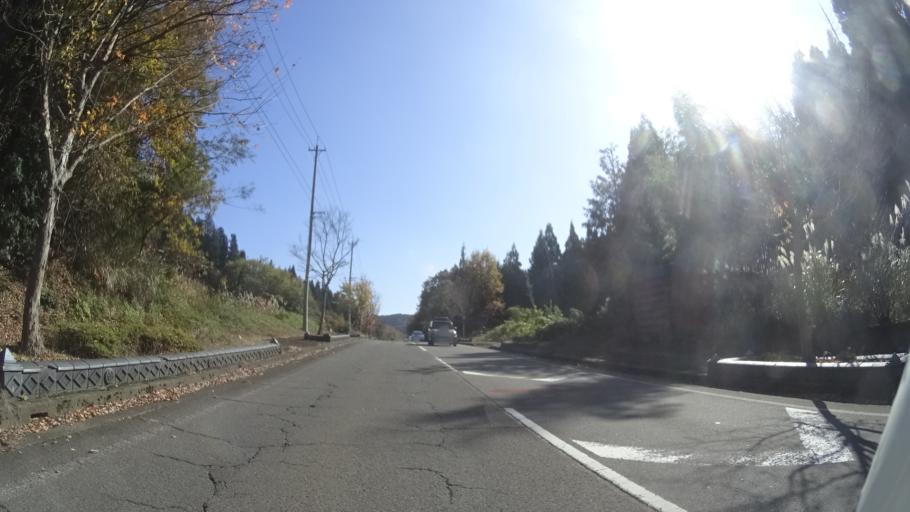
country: JP
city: Asahi
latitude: 35.9611
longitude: 136.0621
